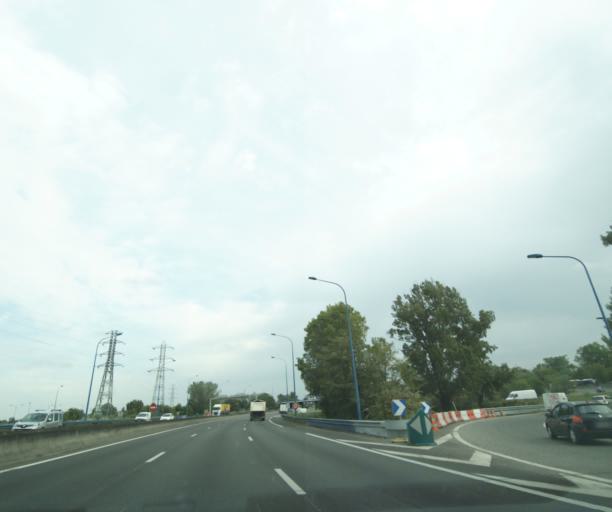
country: FR
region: Midi-Pyrenees
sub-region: Departement de la Haute-Garonne
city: Blagnac
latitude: 43.6212
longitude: 1.4181
